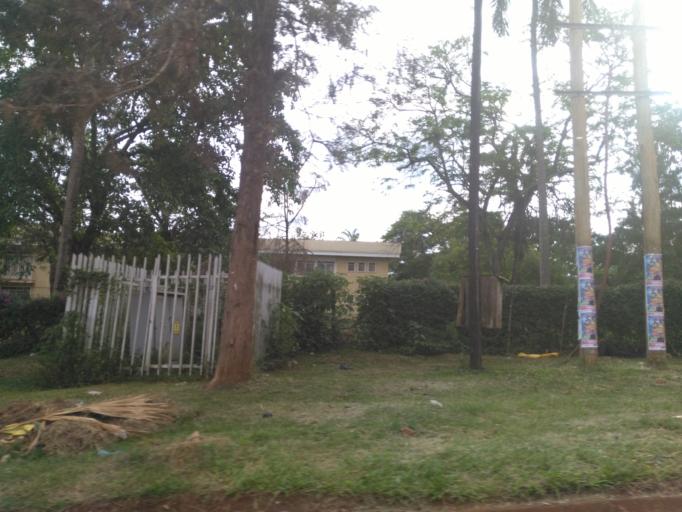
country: UG
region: Eastern Region
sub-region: Jinja District
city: Jinja
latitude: 0.4230
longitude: 33.2071
